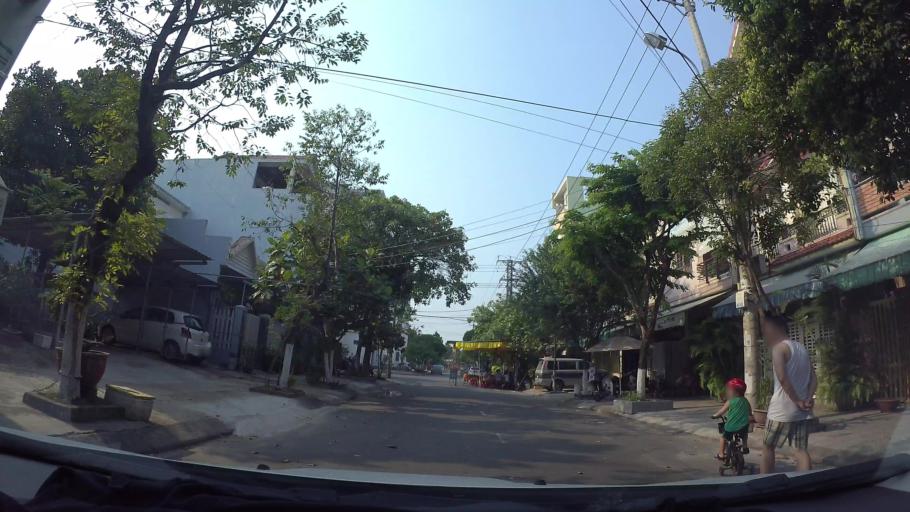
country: VN
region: Da Nang
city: Cam Le
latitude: 16.0221
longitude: 108.2089
